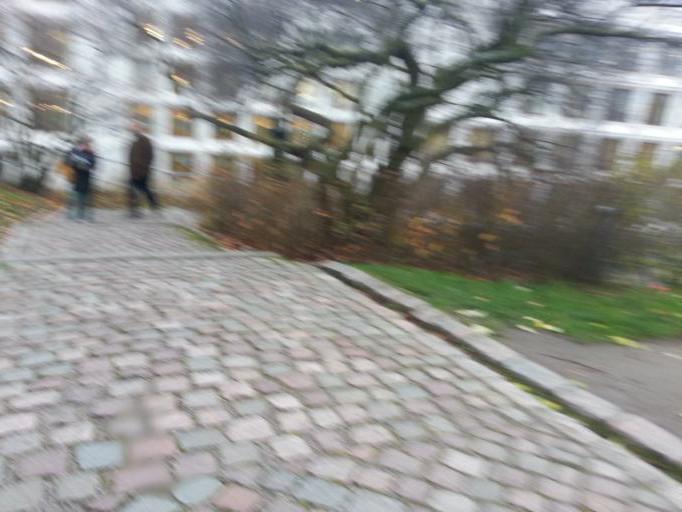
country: FI
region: Uusimaa
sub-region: Helsinki
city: Helsinki
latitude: 60.1682
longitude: 24.9592
